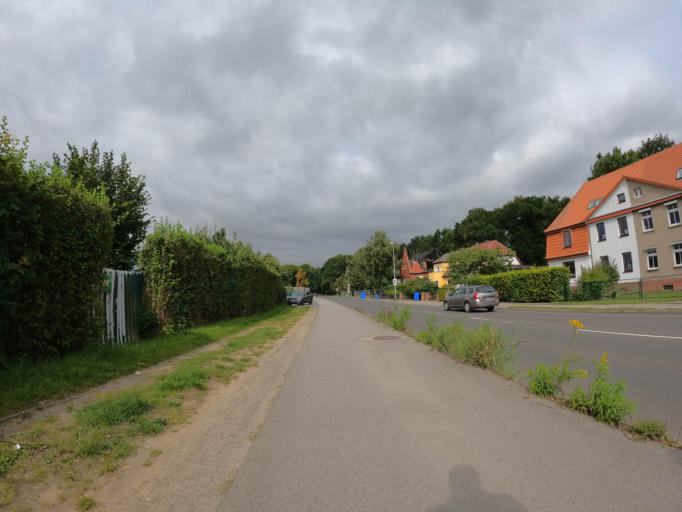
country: DE
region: Mecklenburg-Vorpommern
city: Stralsund
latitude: 54.3142
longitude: 13.0563
